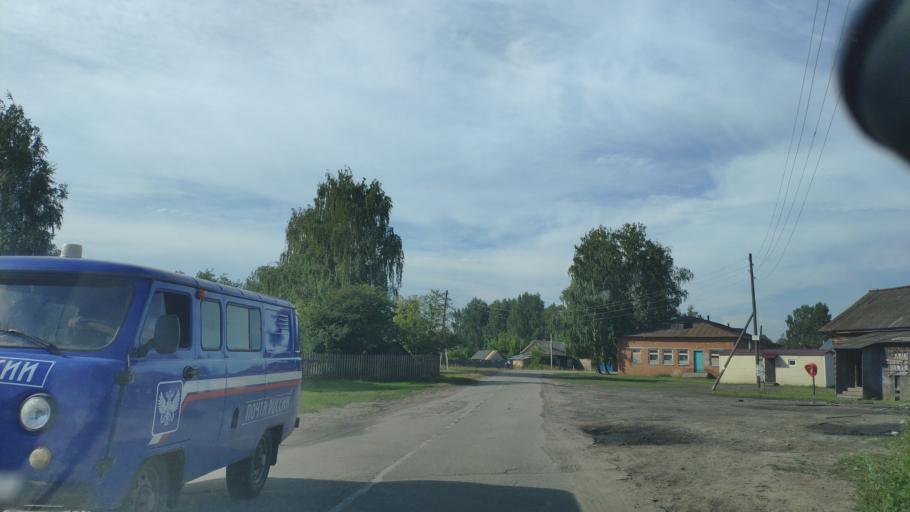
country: RU
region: Nizjnij Novgorod
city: Vorotynets
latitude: 56.1873
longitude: 45.7800
